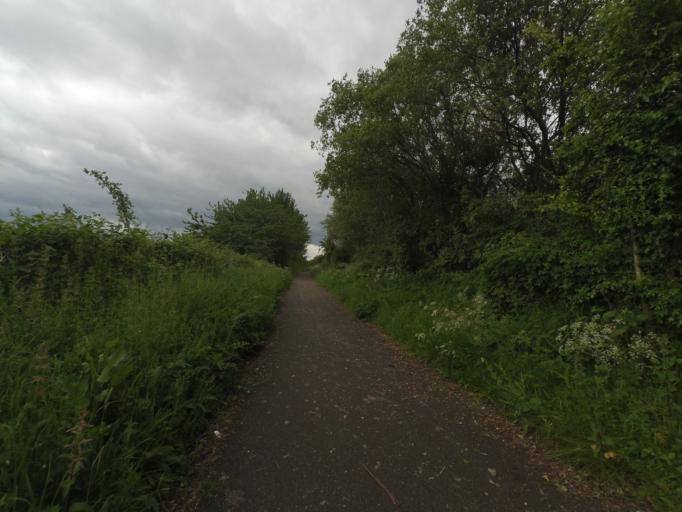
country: GB
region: Scotland
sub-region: East Lothian
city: Musselburgh
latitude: 55.9214
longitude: -3.0342
